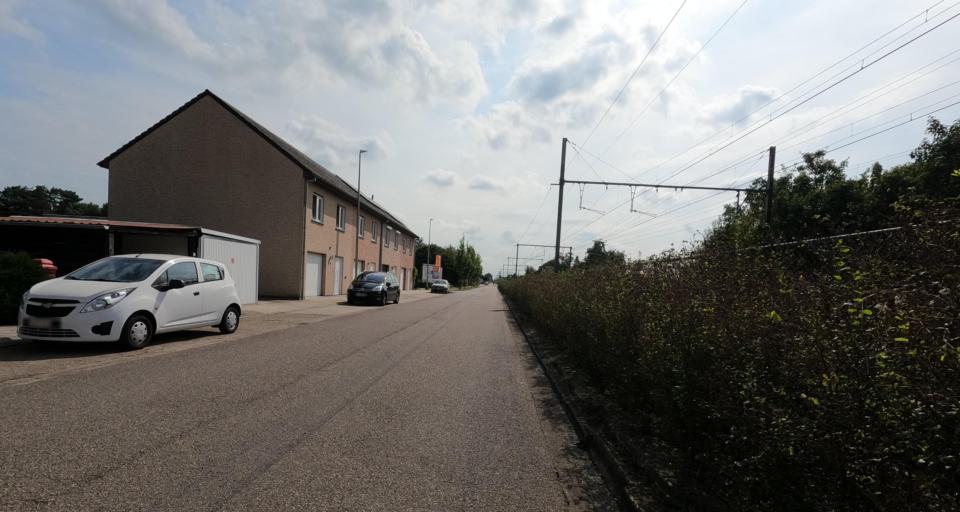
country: BE
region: Flanders
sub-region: Provincie Antwerpen
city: Essen
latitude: 51.4573
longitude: 4.4532
